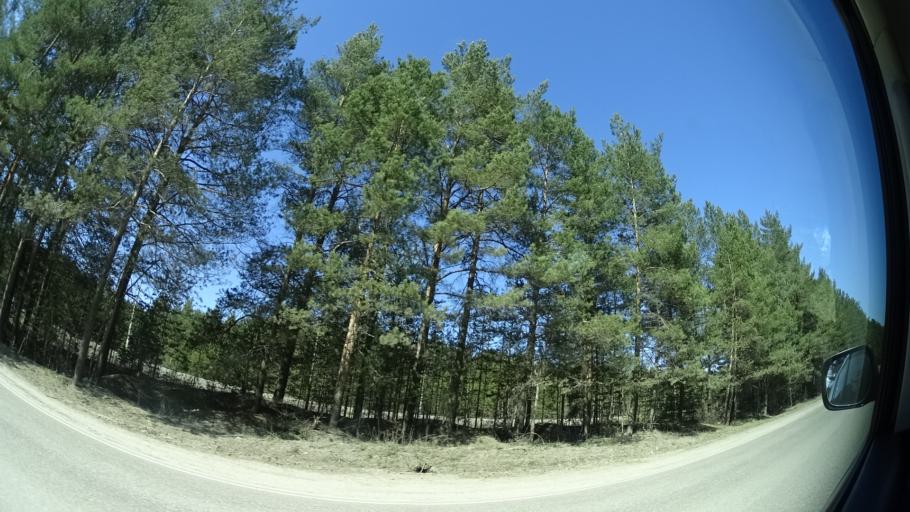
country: RU
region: Perm
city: Perm
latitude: 58.0565
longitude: 56.2481
